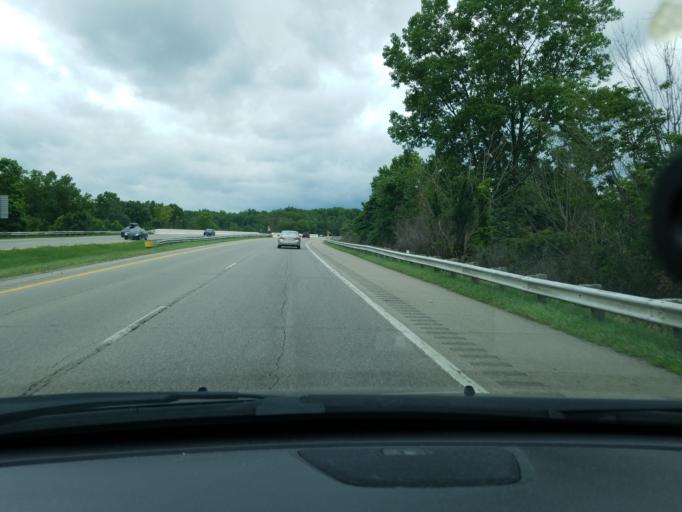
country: US
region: Ohio
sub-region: Lorain County
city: Amherst
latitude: 41.4047
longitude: -82.2579
